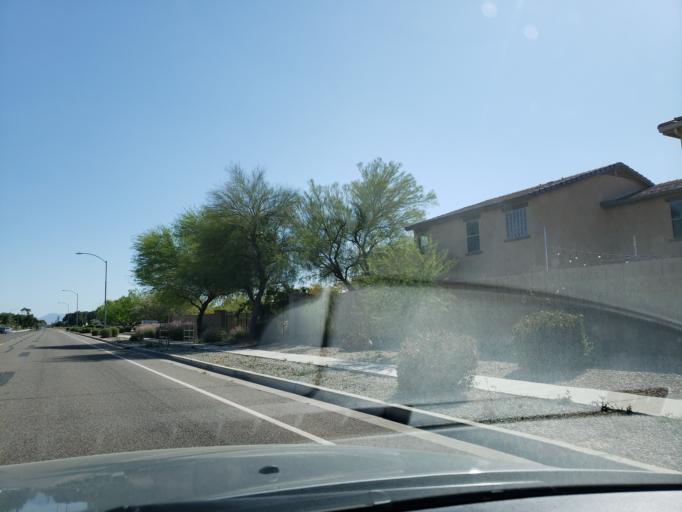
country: US
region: Arizona
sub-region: Maricopa County
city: Glendale
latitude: 33.5619
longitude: -112.1950
